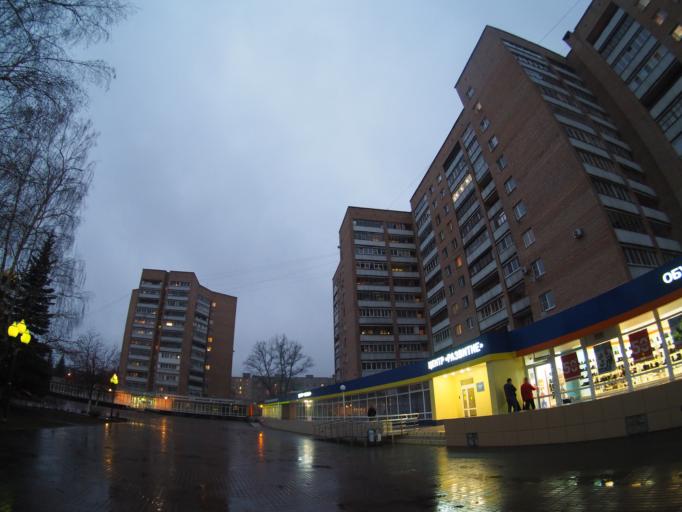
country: RU
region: Moskovskaya
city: Stupino
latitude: 54.8868
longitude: 38.0673
